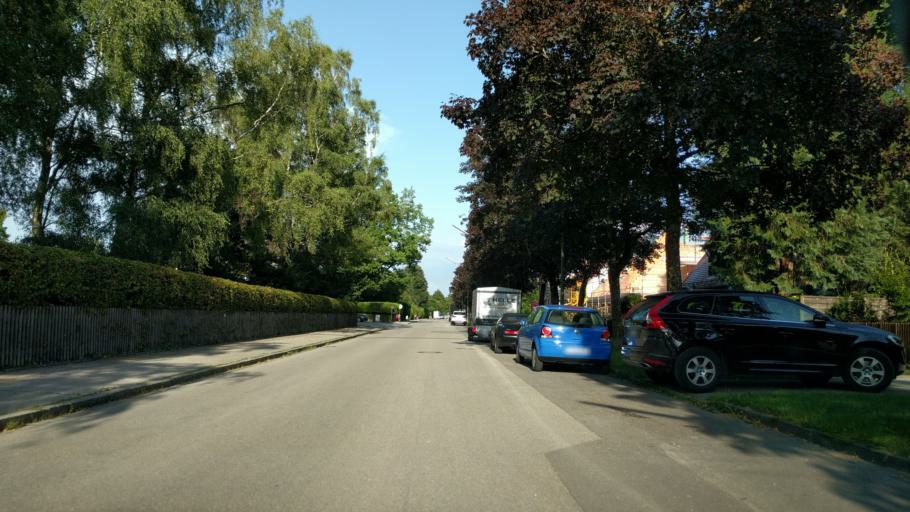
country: DE
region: Bavaria
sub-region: Upper Bavaria
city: Grunwald
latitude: 48.0409
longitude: 11.5308
